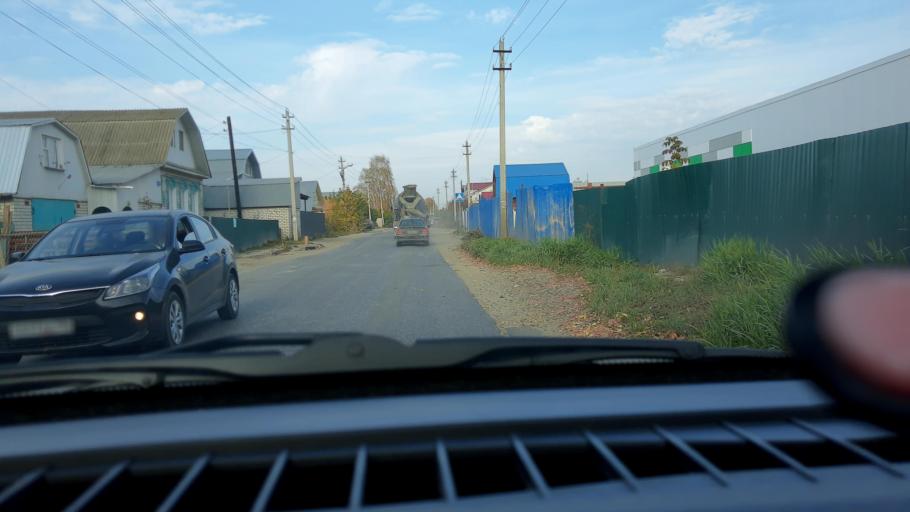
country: RU
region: Nizjnij Novgorod
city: Neklyudovo
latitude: 56.4078
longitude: 43.9806
